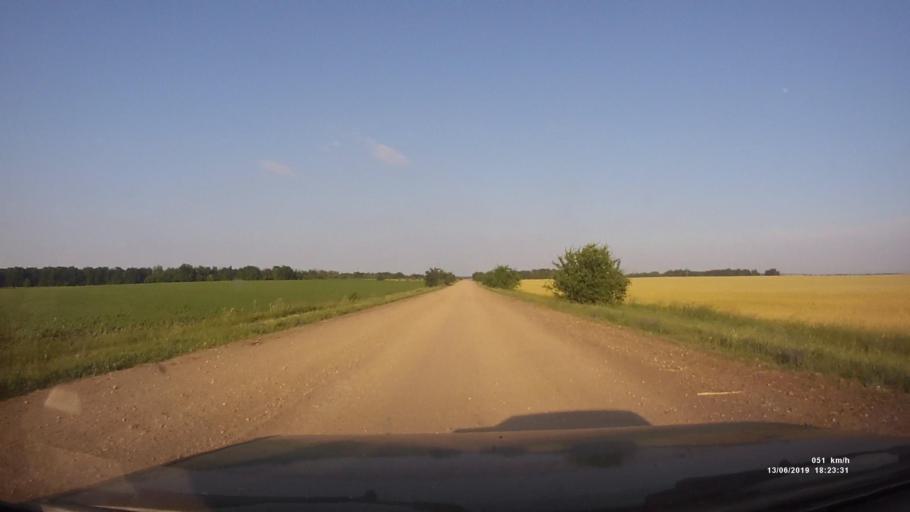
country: RU
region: Rostov
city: Kazanskaya
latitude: 49.8526
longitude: 41.2788
